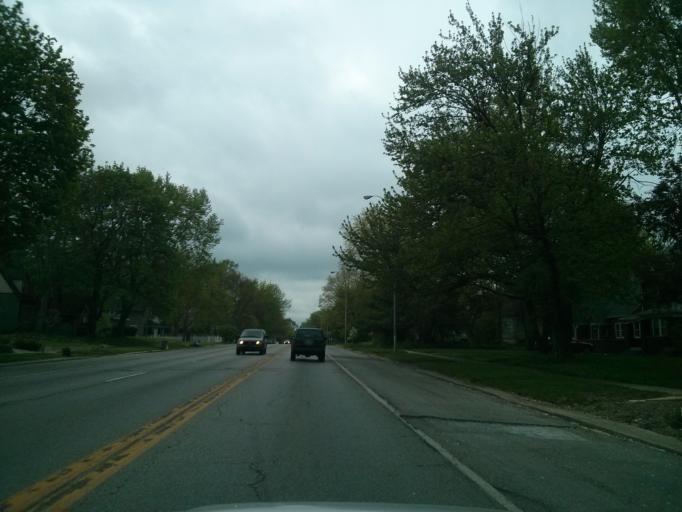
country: US
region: Indiana
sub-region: Marion County
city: Broad Ripple
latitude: 39.8572
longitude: -86.1460
